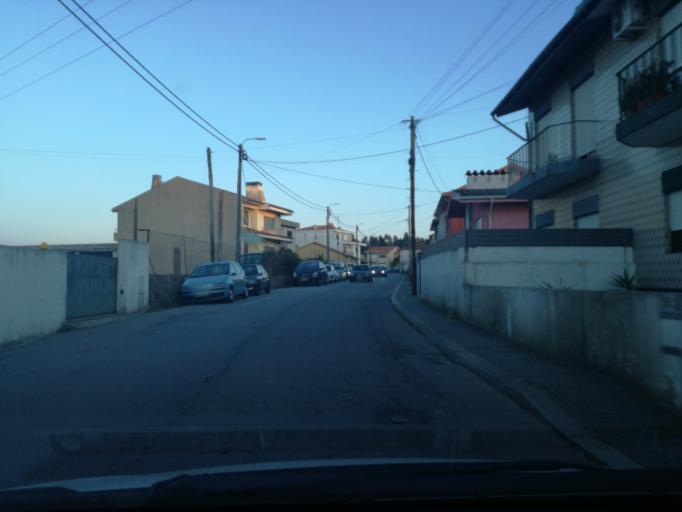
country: PT
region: Porto
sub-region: Maia
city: Anta
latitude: 41.2661
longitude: -8.6355
